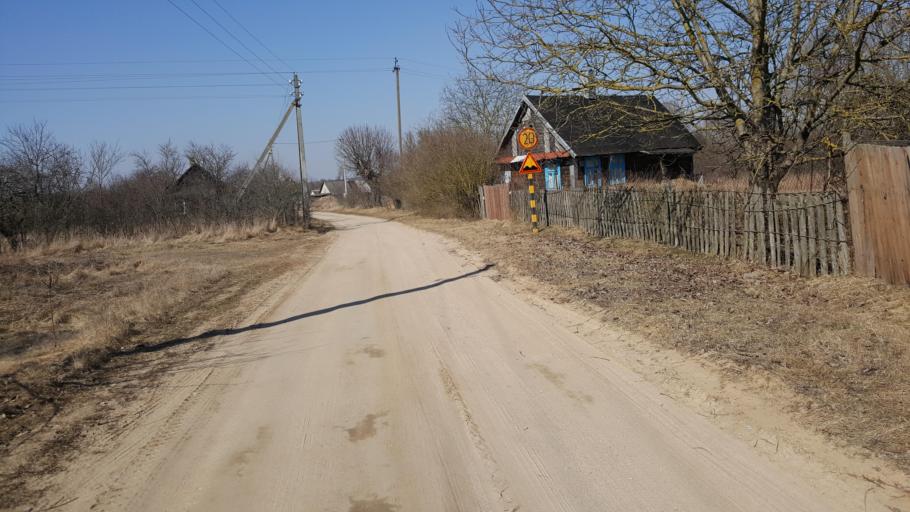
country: BY
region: Brest
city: Kamyanyets
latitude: 52.3537
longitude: 23.7544
